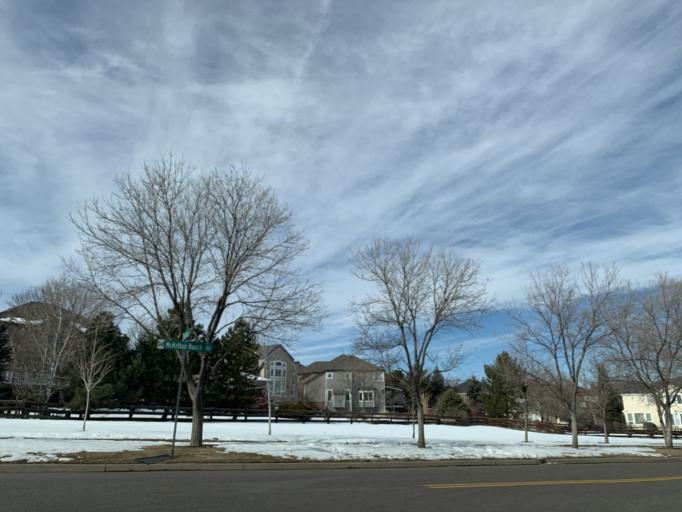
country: US
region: Colorado
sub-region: Douglas County
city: Carriage Club
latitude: 39.5194
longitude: -104.9155
